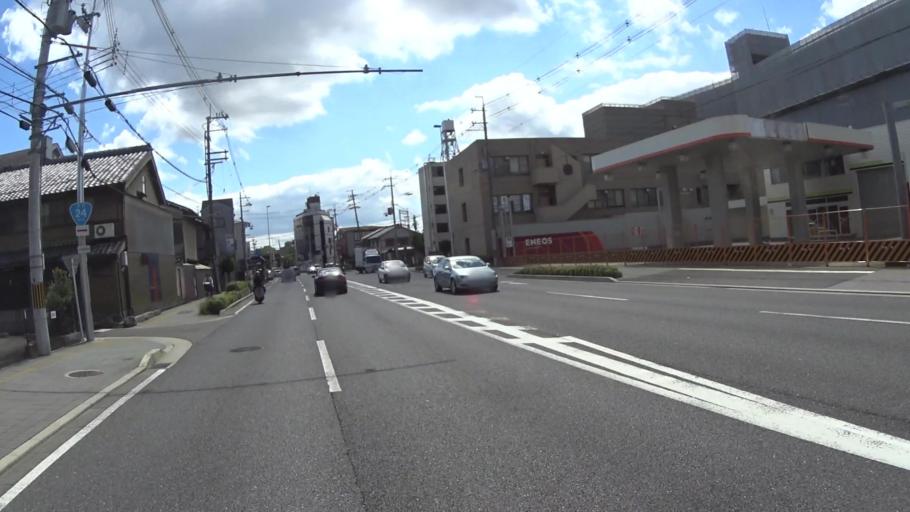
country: JP
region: Kyoto
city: Muko
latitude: 34.9502
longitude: 135.7587
